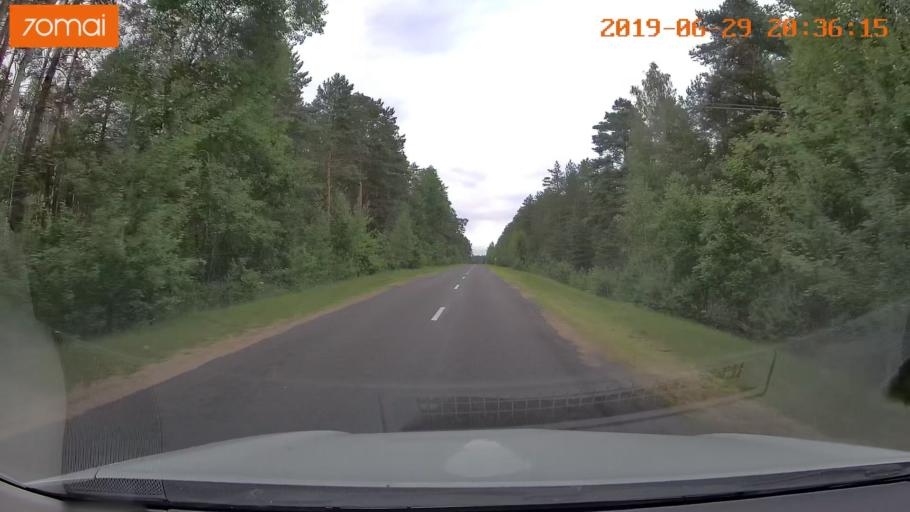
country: BY
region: Brest
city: Hantsavichy
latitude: 52.5241
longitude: 26.3570
